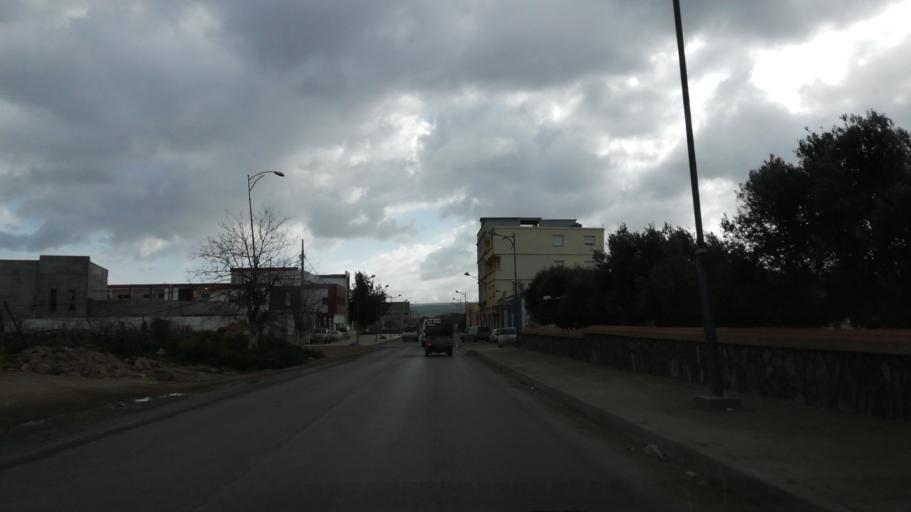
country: DZ
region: Oran
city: Sidi ech Chahmi
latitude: 35.6575
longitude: -0.5293
